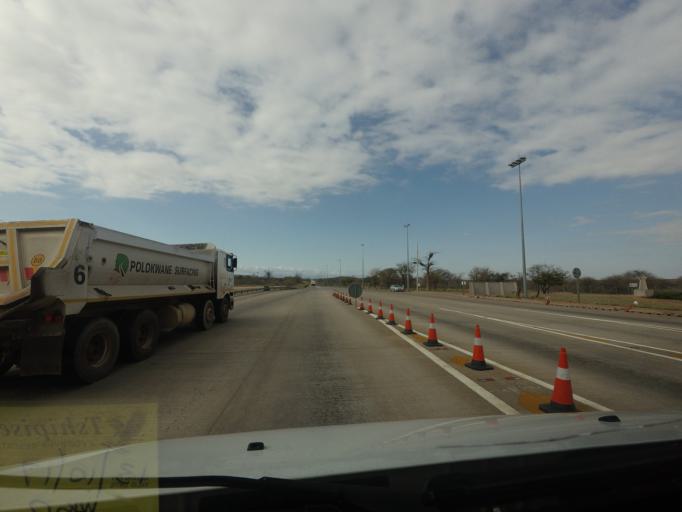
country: ZA
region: Limpopo
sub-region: Vhembe District Municipality
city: Messina
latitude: -22.6473
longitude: 29.9181
